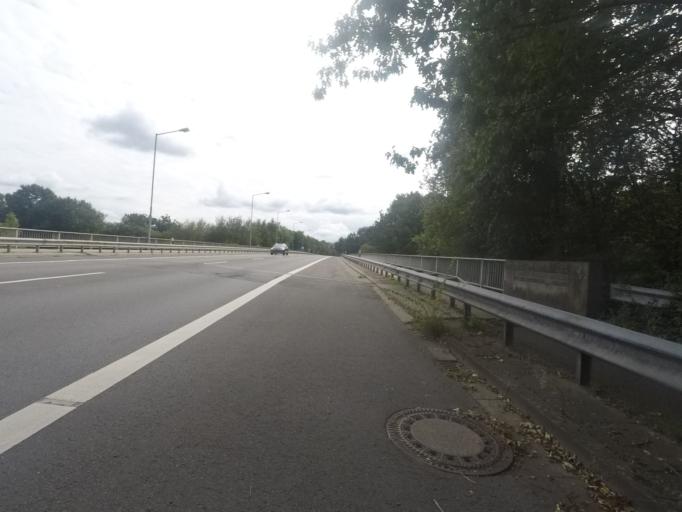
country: DE
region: North Rhine-Westphalia
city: Loehne
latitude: 52.2041
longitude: 8.7242
